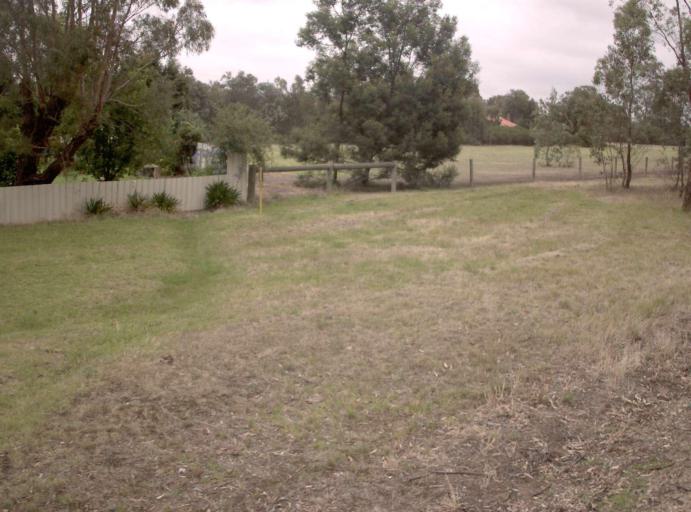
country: AU
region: Victoria
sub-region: Wellington
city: Heyfield
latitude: -37.9721
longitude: 146.7804
